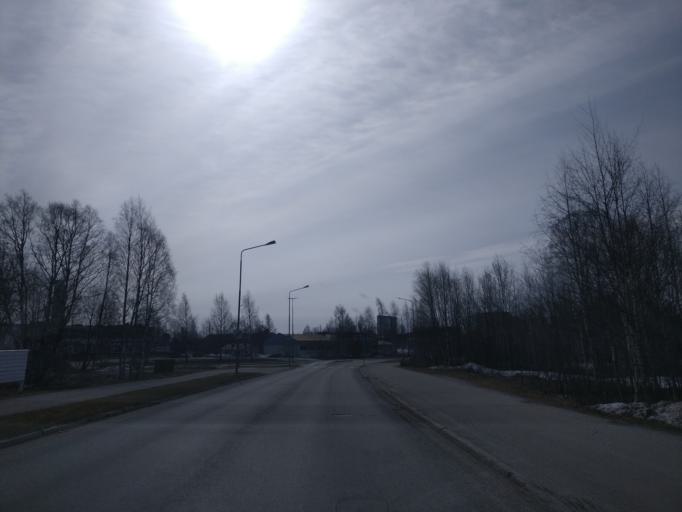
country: FI
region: Lapland
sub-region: Kemi-Tornio
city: Kemi
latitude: 65.7440
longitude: 24.5656
